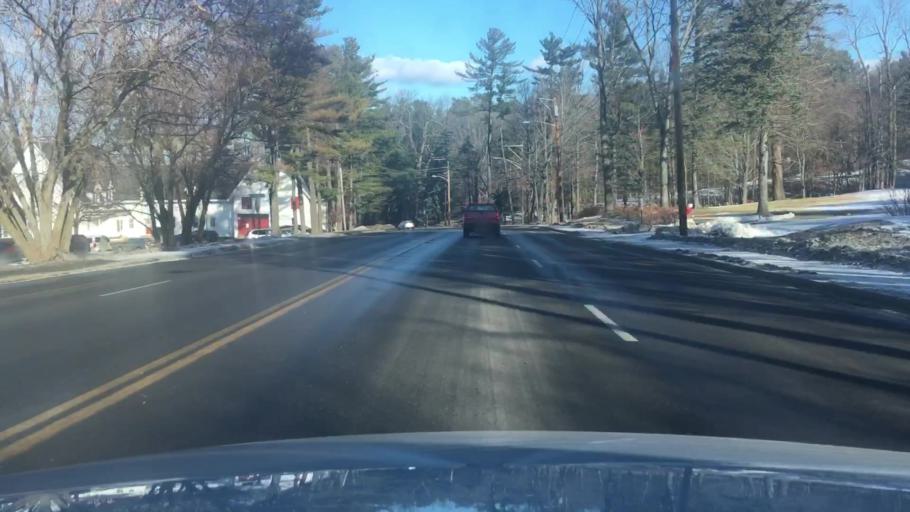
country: US
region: Maine
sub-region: Kennebec County
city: Augusta
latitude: 44.3117
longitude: -69.7644
